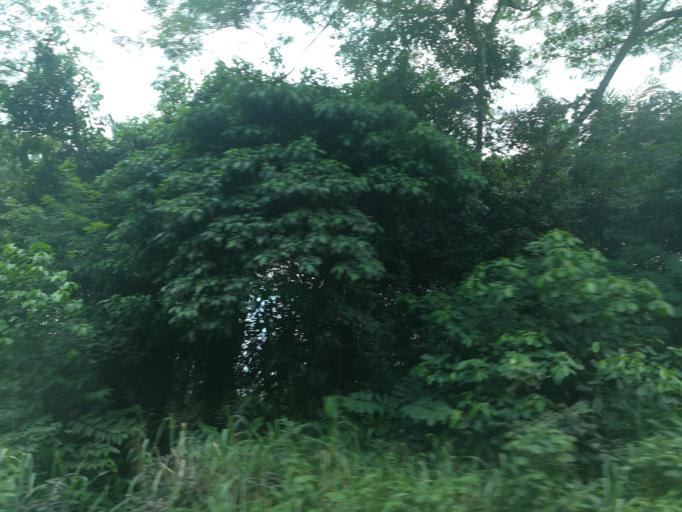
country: NG
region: Lagos
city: Ejirin
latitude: 6.6459
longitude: 3.7229
